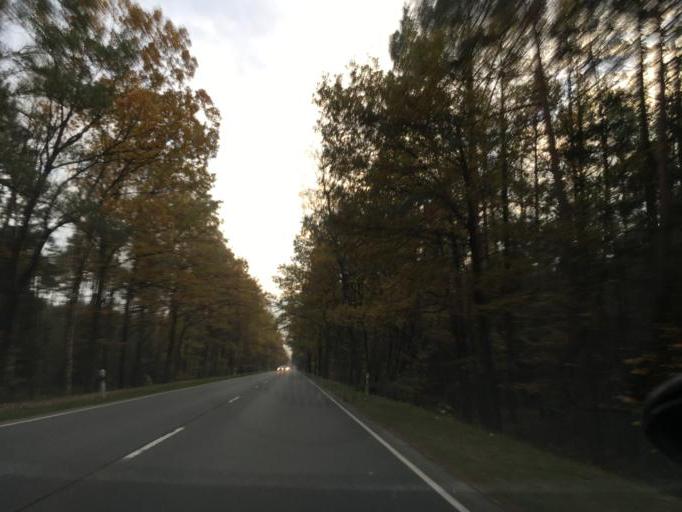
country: DE
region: Lower Saxony
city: Bergen
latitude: 52.7541
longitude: 9.9781
